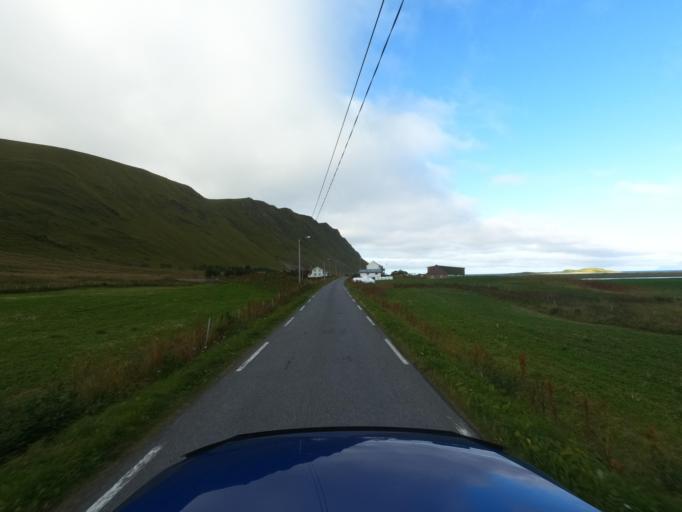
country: NO
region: Nordland
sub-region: Flakstad
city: Ramberg
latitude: 68.0931
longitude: 13.1378
